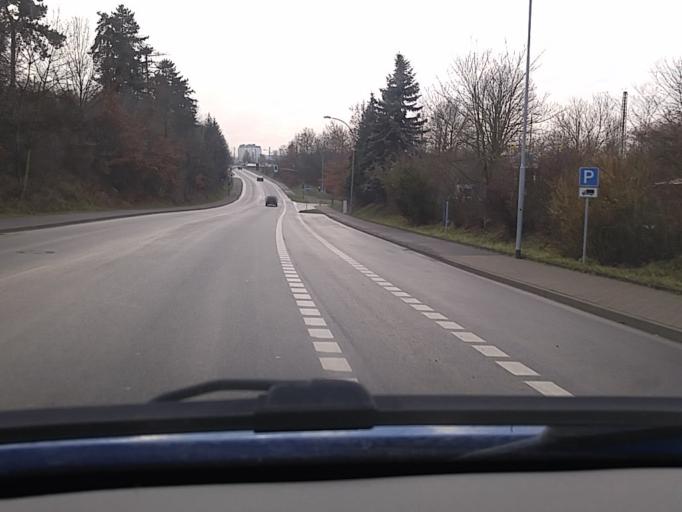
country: DE
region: Hesse
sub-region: Regierungsbezirk Darmstadt
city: Bad Nauheim
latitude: 50.3728
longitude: 8.7490
